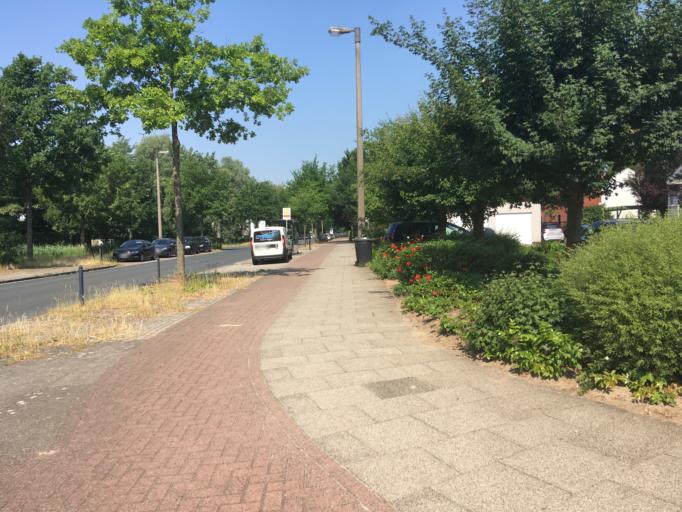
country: DE
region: Lower Saxony
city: Lilienthal
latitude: 53.1098
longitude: 8.8825
